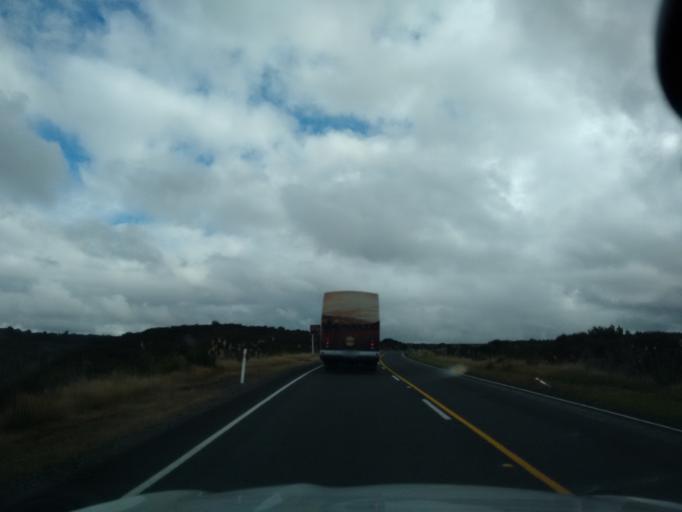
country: NZ
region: Waikato
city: Turangi
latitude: -39.0634
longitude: 175.5762
